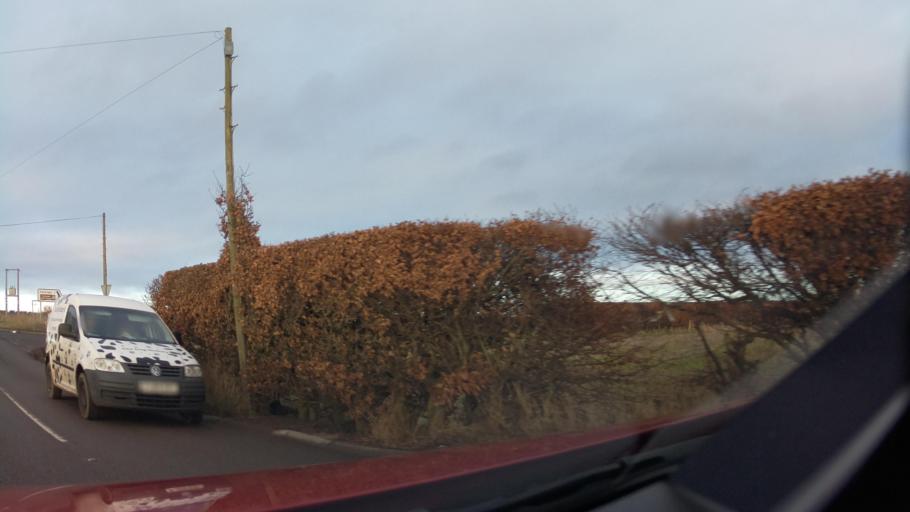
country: GB
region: Scotland
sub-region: Fife
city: Tayport
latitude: 56.5089
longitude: -2.8174
